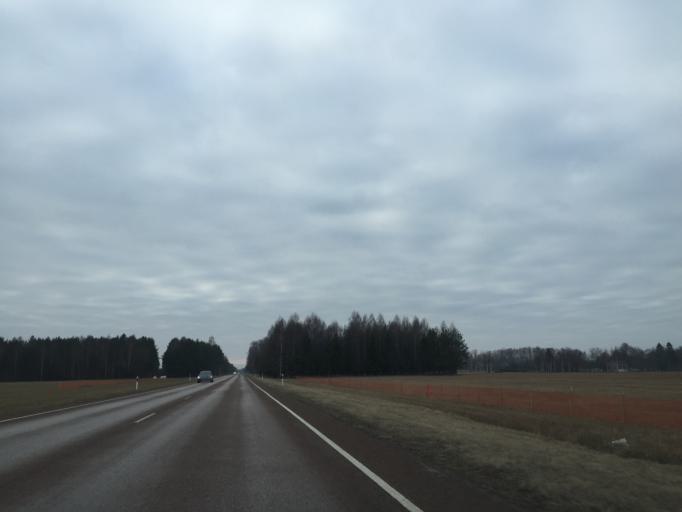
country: EE
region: Saare
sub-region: Orissaare vald
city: Orissaare
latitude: 58.5288
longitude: 23.0079
